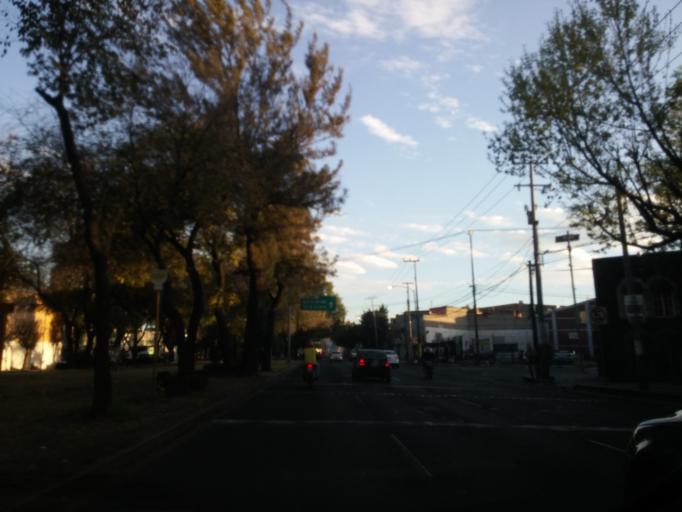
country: MX
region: Mexico City
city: Cuauhtemoc
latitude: 19.4598
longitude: -99.1700
